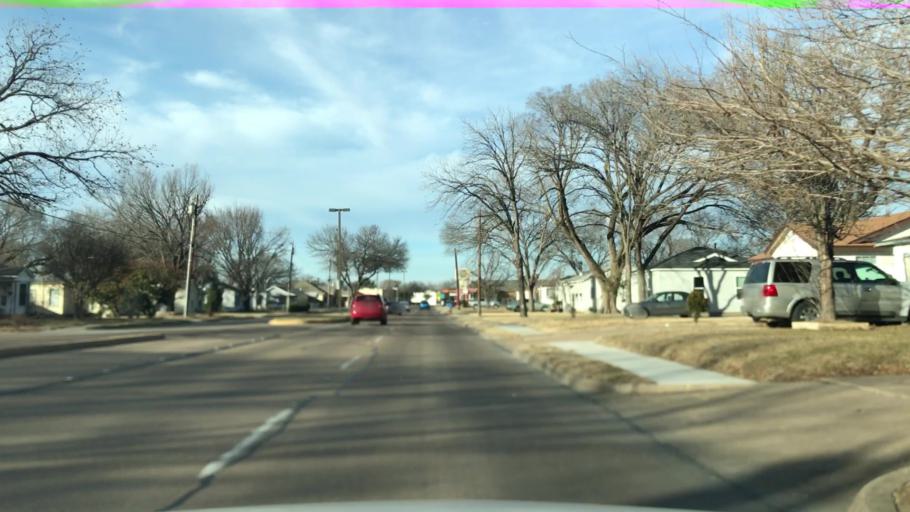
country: US
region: Texas
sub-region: Dallas County
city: Irving
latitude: 32.8183
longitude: -96.9596
